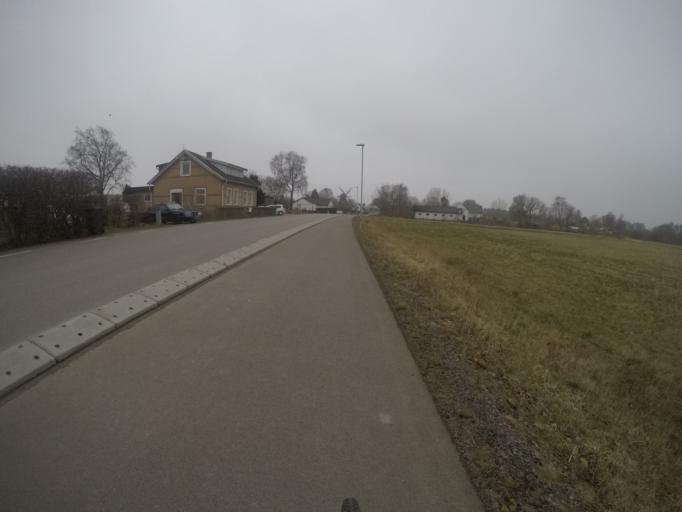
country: SE
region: Skane
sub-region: Angelholms Kommun
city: Vejbystrand
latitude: 56.2208
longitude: 12.7191
